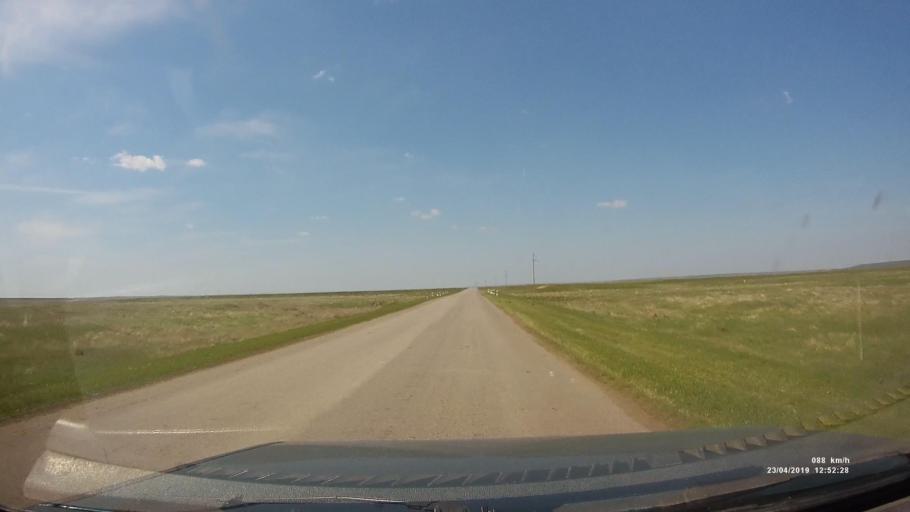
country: RU
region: Kalmykiya
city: Yashalta
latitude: 46.5643
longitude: 42.6100
